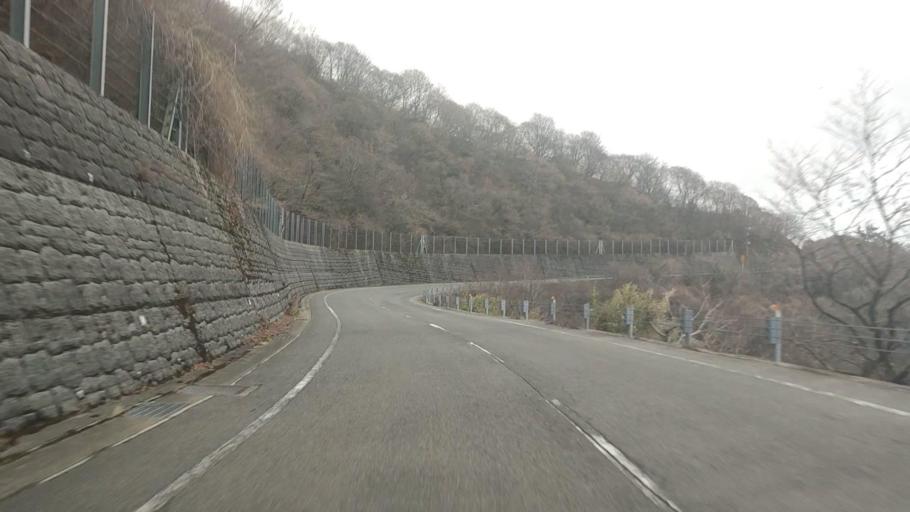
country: JP
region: Nagasaki
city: Shimabara
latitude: 32.7572
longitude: 130.2761
